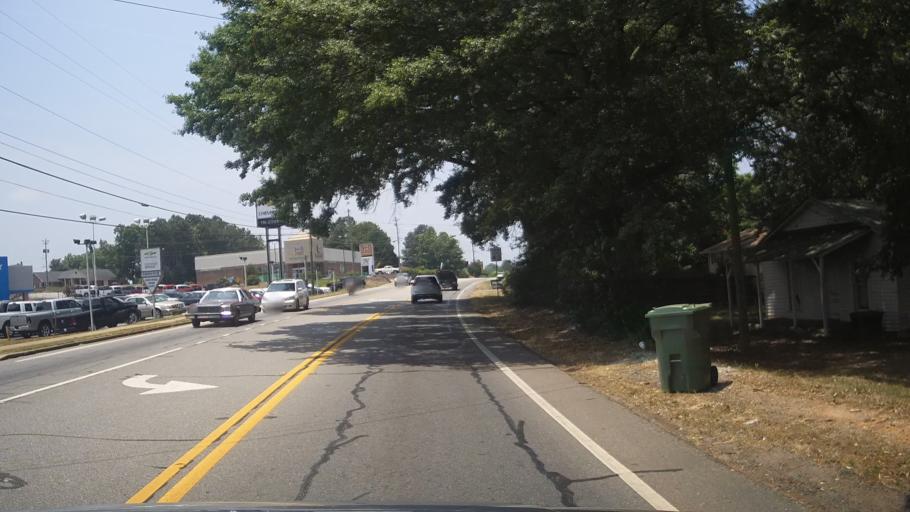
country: US
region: Georgia
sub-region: Hart County
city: Royston
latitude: 34.2845
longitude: -83.1225
